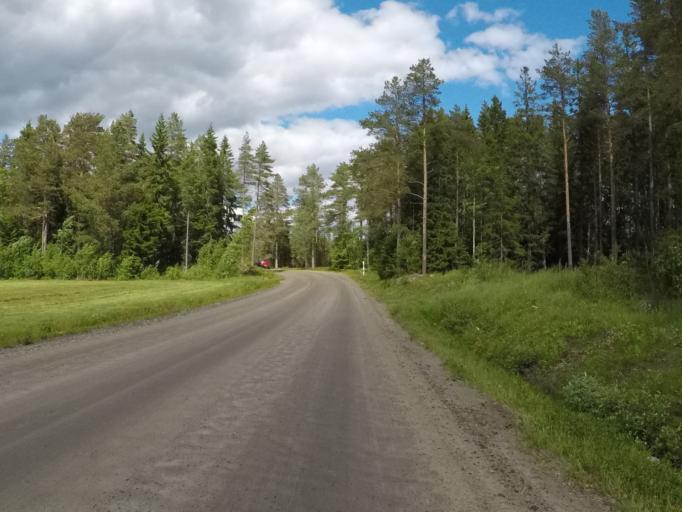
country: SE
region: Vaesterbotten
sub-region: Robertsfors Kommun
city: Robertsfors
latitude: 64.0141
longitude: 20.9016
